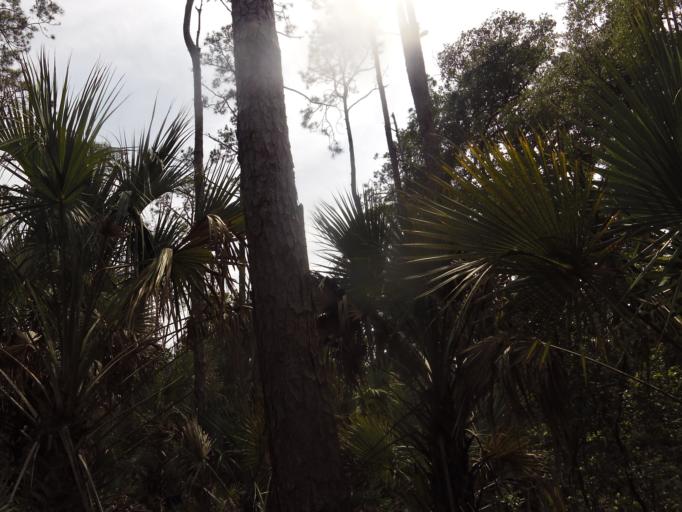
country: US
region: Florida
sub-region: Flagler County
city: Flagler Beach
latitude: 29.4053
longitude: -81.1231
